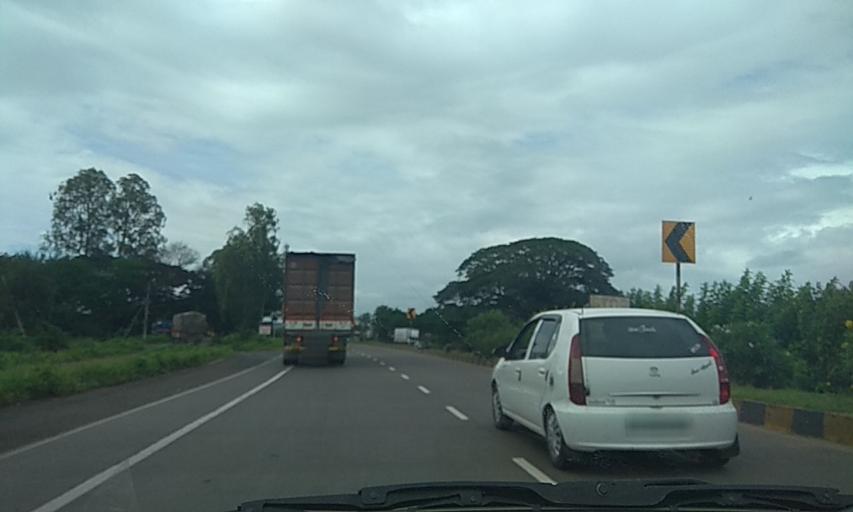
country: IN
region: Maharashtra
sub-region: Kolhapur
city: Kagal
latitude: 16.5669
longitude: 74.3162
